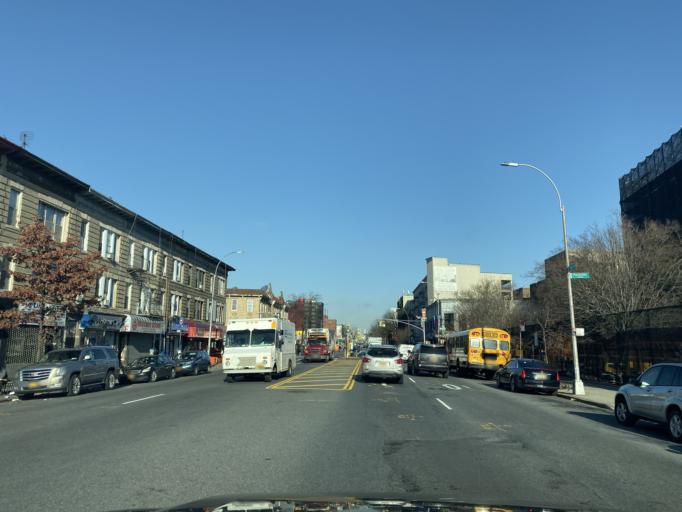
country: US
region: New York
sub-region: Kings County
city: Brooklyn
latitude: 40.6330
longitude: -73.9669
